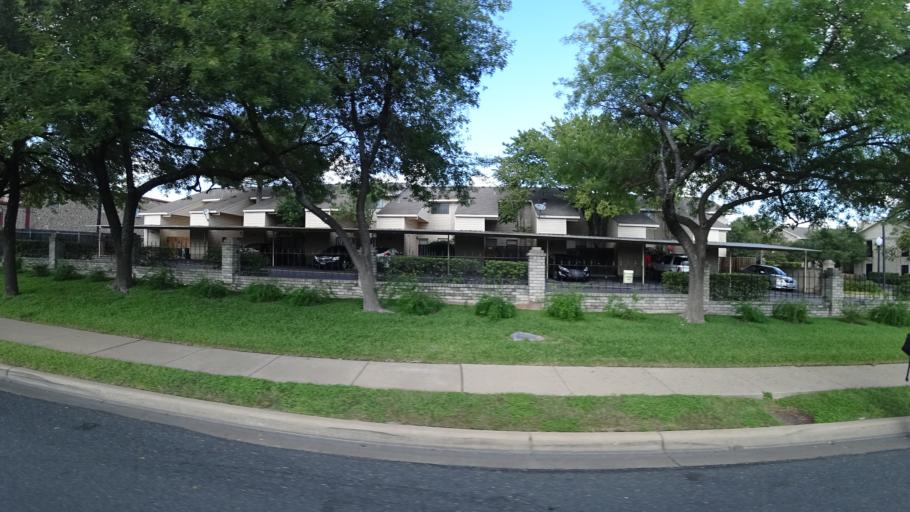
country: US
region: Texas
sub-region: Travis County
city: Austin
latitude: 30.3558
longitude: -97.7137
